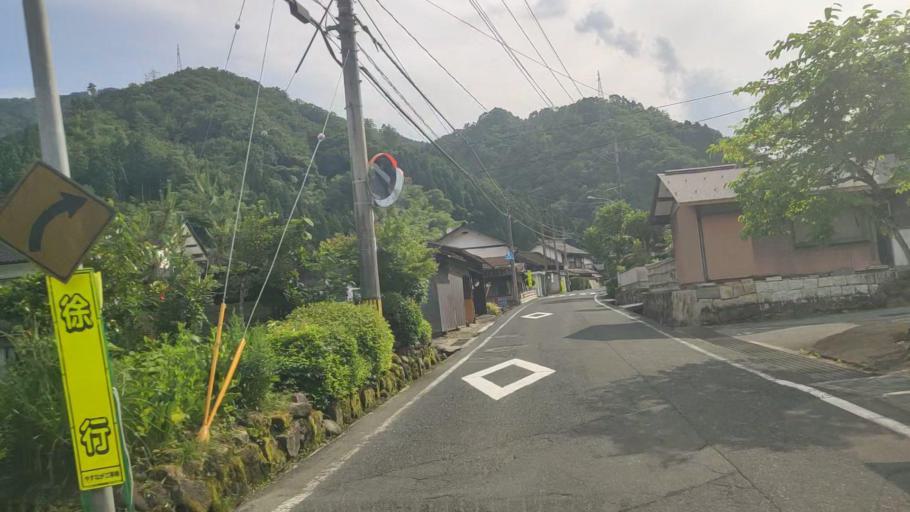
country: JP
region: Tottori
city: Tottori
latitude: 35.3350
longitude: 134.1424
